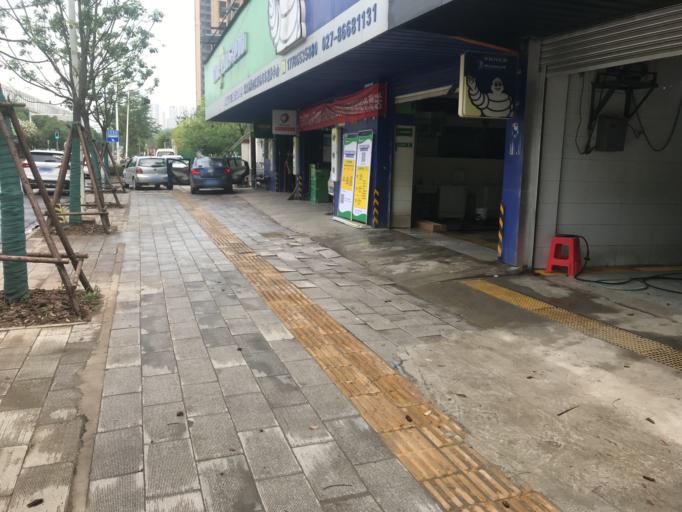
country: CN
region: Hubei
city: Heping
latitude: 30.6064
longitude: 114.3612
